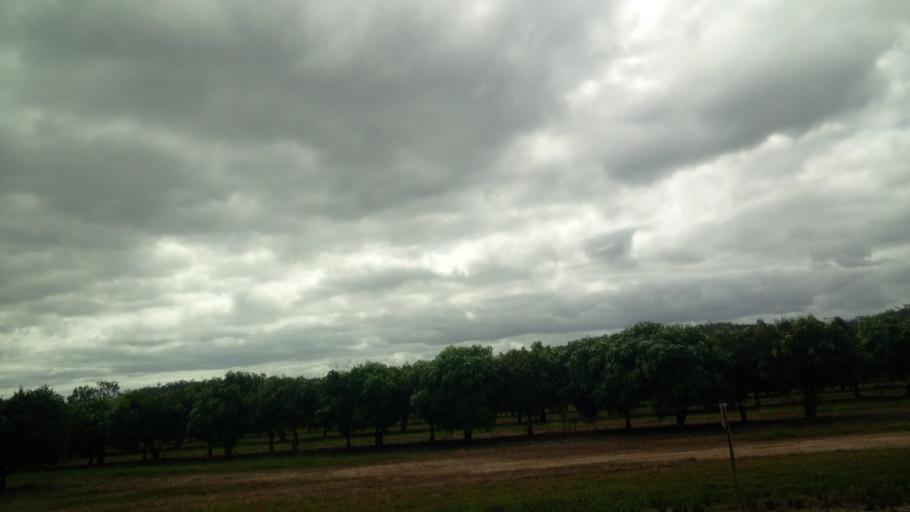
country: AU
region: Queensland
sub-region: Tablelands
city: Mareeba
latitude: -16.9791
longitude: 145.4735
